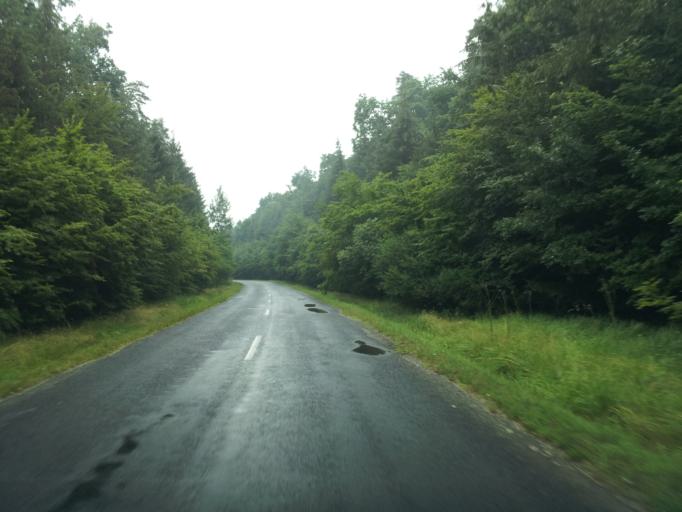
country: HU
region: Zala
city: Zalalovo
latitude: 46.9303
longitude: 16.5660
